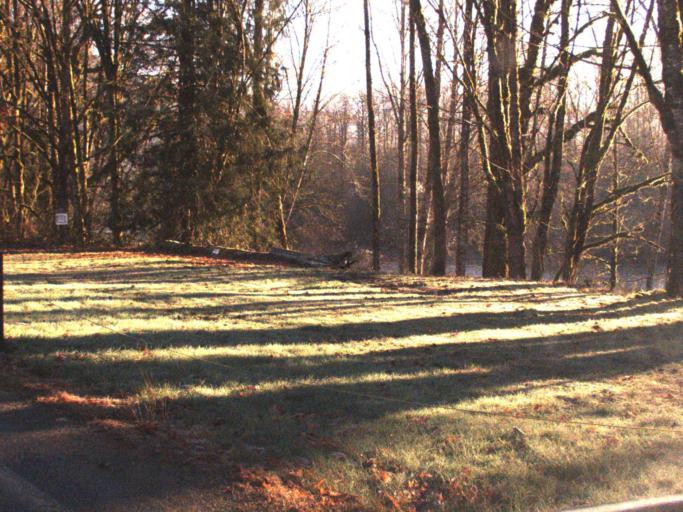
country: US
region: Washington
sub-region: Snohomish County
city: Darrington
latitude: 48.5262
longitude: -121.4538
